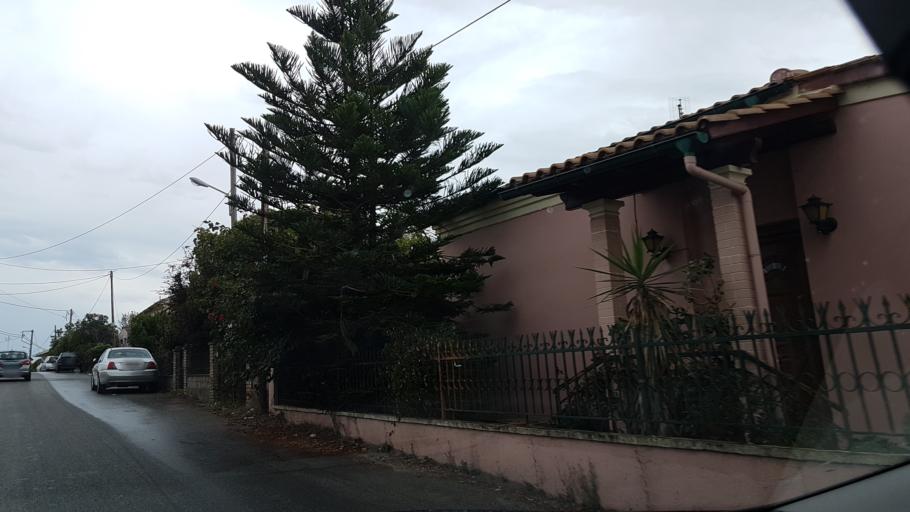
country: GR
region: Ionian Islands
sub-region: Nomos Kerkyras
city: Kerkyra
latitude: 39.6144
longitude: 19.9099
